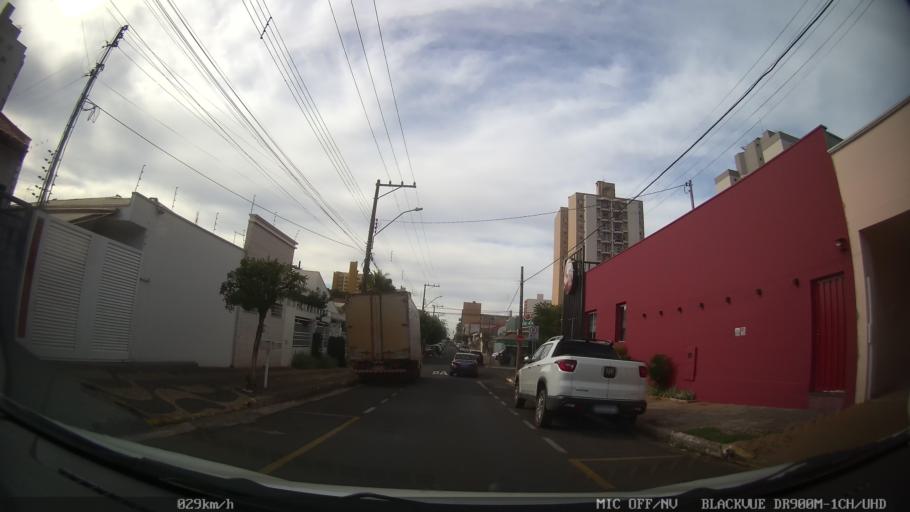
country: BR
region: Sao Paulo
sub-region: Catanduva
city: Catanduva
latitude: -21.1384
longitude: -48.9767
